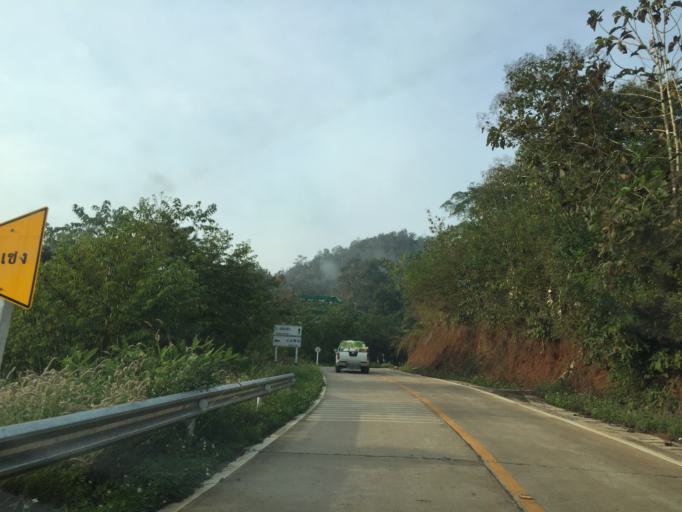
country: TH
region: Chiang Mai
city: Samoeng
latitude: 18.9670
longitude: 98.7172
